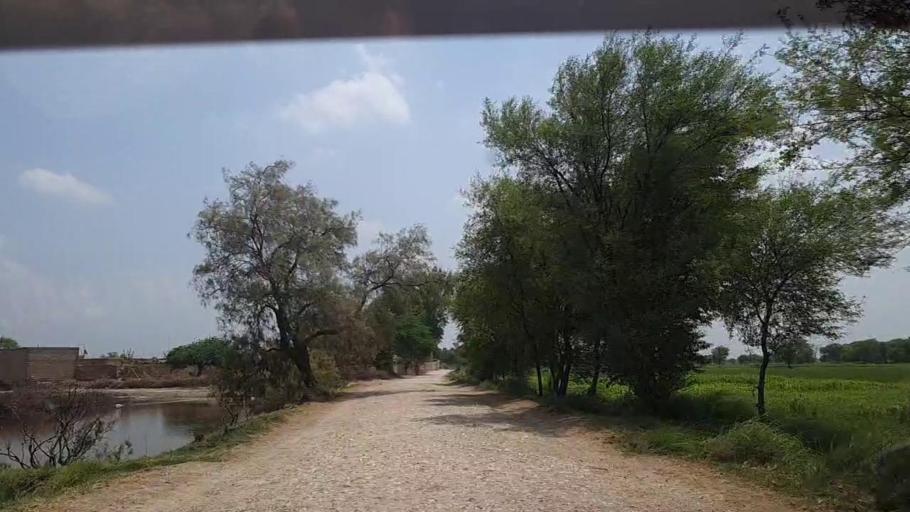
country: PK
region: Sindh
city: Khanpur
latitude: 27.8881
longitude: 69.4052
